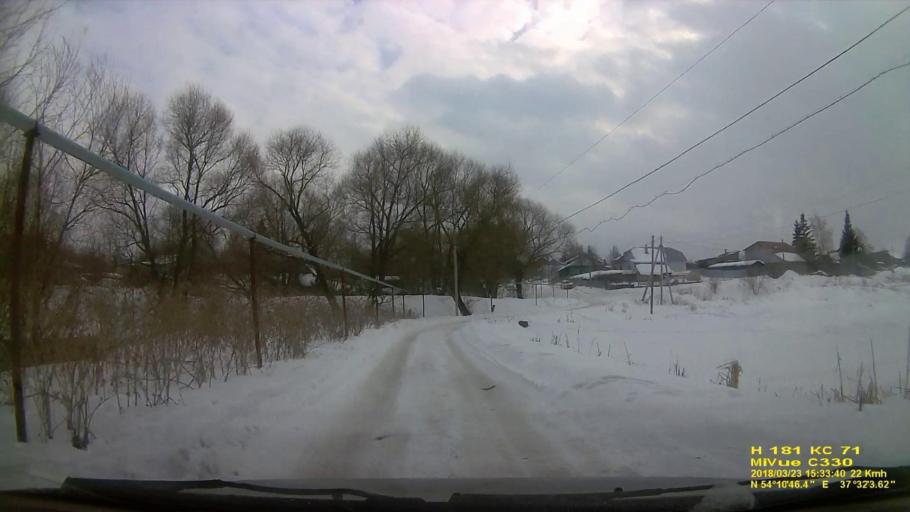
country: RU
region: Tula
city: Kosaya Gora
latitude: 54.1791
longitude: 37.5352
